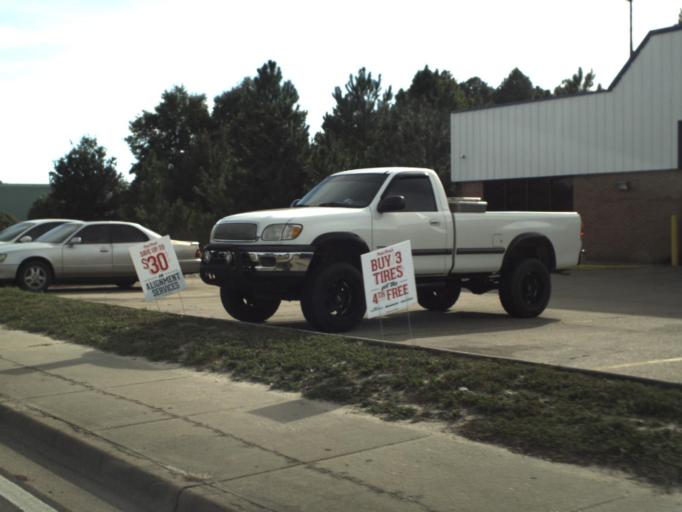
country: US
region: Florida
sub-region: Bay County
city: Springfield
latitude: 30.1481
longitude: -85.5913
